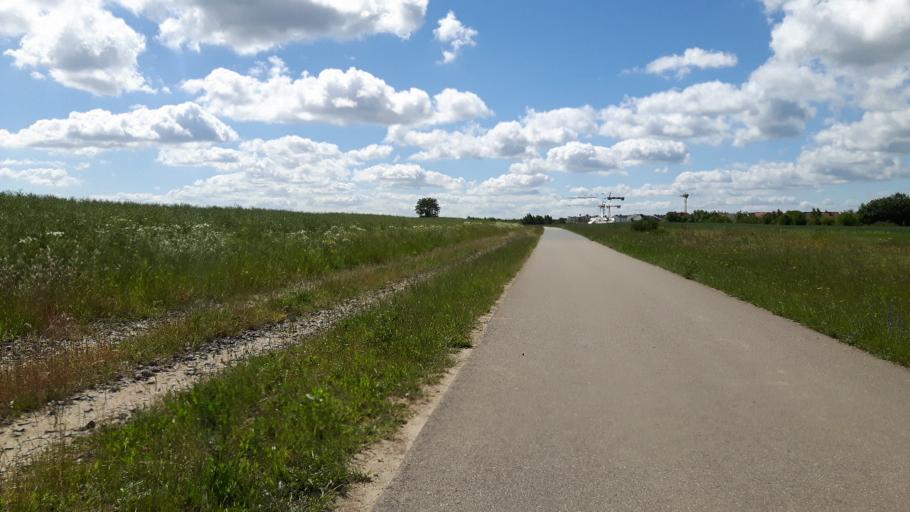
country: PL
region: Pomeranian Voivodeship
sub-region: Powiat pucki
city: Kosakowo
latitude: 54.5768
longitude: 18.4961
